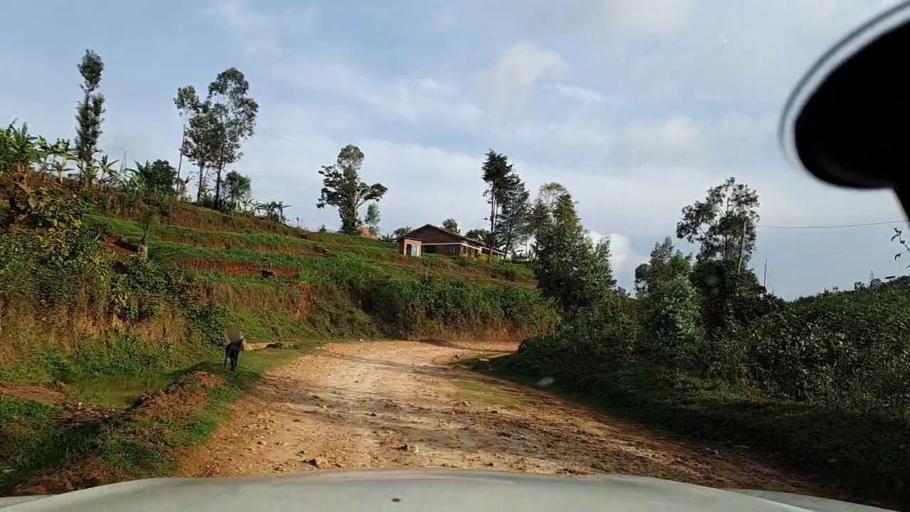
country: RW
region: Southern Province
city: Gitarama
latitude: -2.1845
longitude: 29.5643
